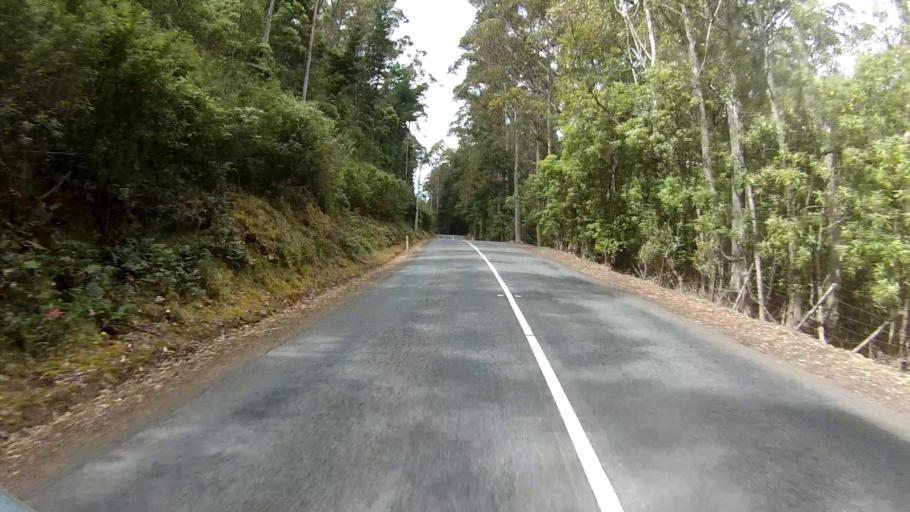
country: AU
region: Tasmania
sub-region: Kingborough
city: Kingston
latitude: -42.9485
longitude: 147.2341
